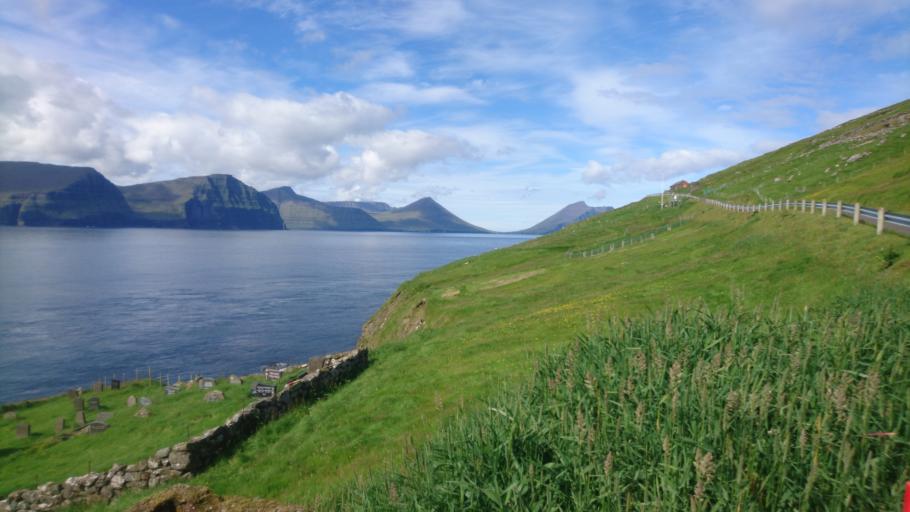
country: FO
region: Nordoyar
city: Klaksvik
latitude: 62.3187
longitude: -6.3178
